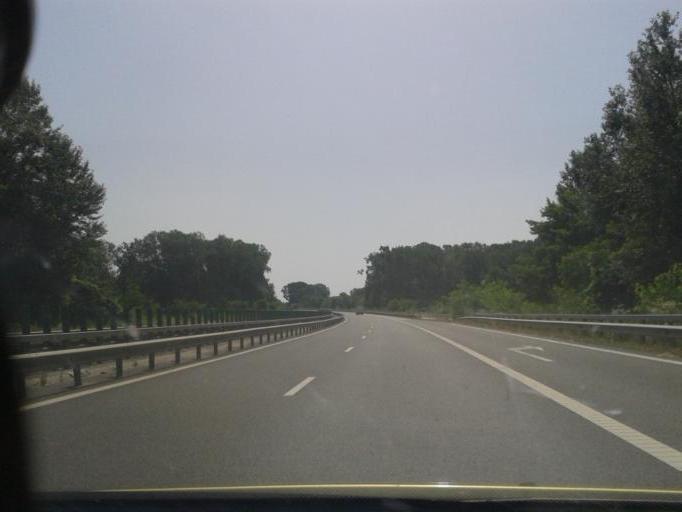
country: RO
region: Prahova
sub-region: Comuna Rafov
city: Rafov
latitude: 44.8609
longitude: 26.1538
